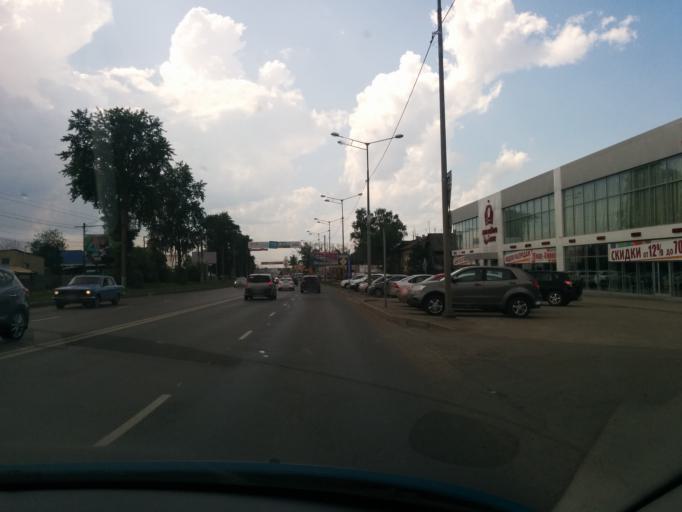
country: RU
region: Perm
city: Kondratovo
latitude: 57.9662
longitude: 56.1448
